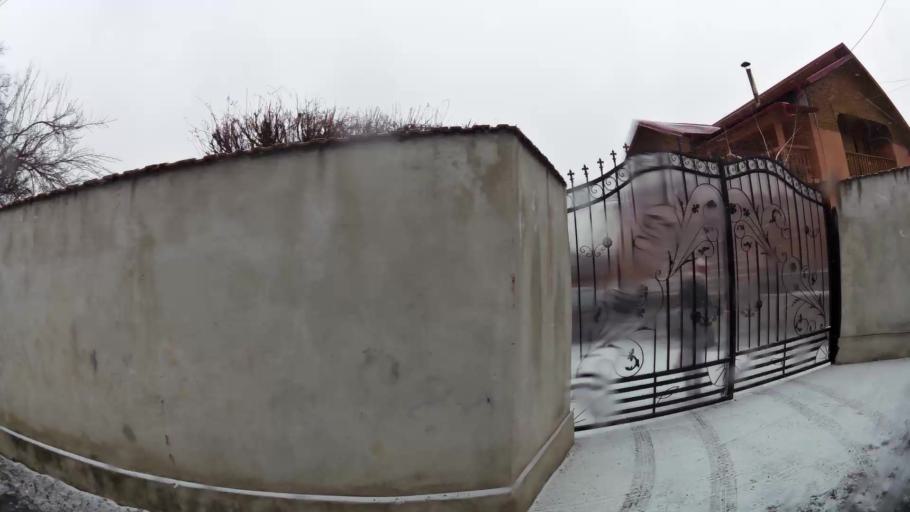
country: RO
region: Dambovita
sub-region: Comuna Ulmi
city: Ulmi
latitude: 44.9114
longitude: 25.4814
